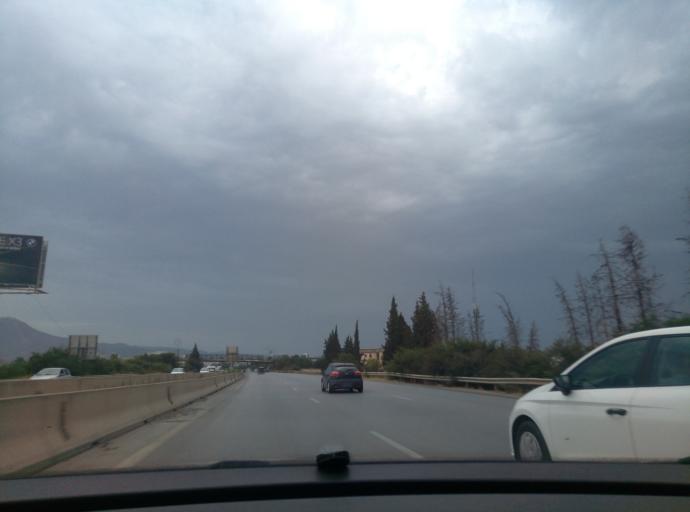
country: TN
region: Tunis
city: La Sebala du Mornag
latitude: 36.7186
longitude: 10.2664
